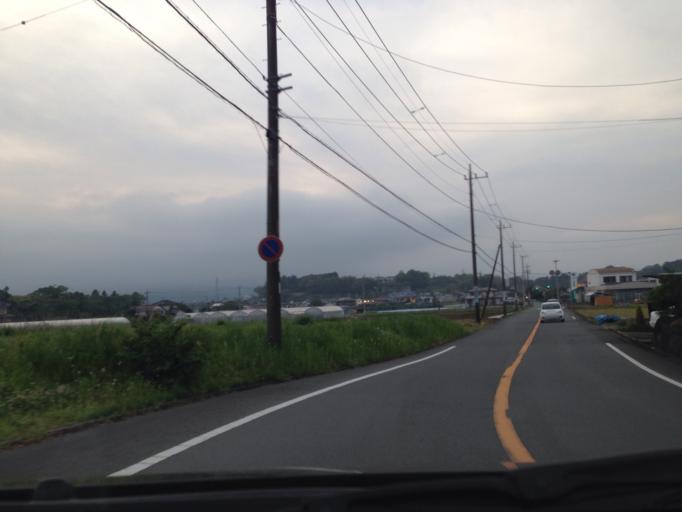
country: JP
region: Shizuoka
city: Mishima
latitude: 35.1662
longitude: 138.9235
